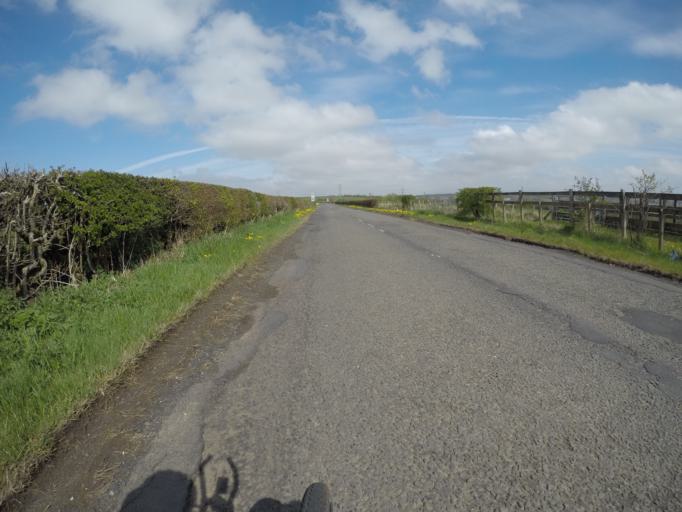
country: GB
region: Scotland
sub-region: East Ayrshire
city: Stewarton
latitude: 55.7000
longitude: -4.4835
